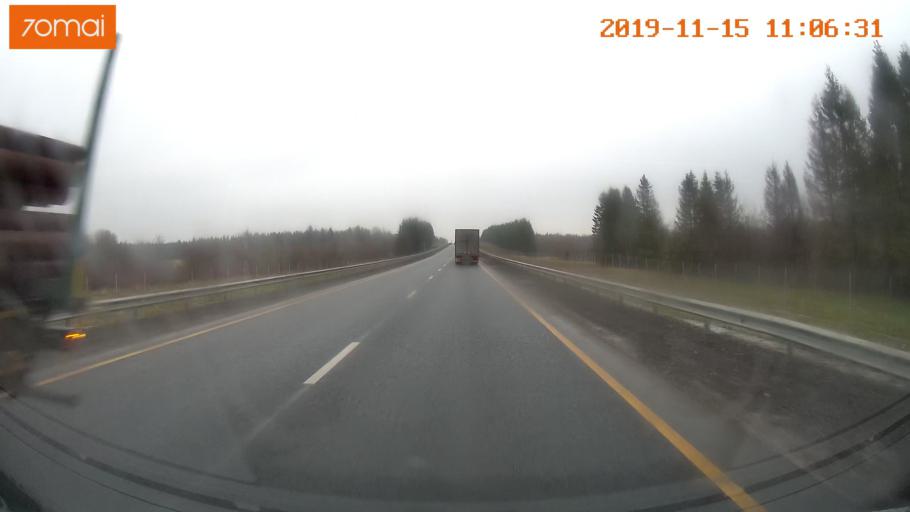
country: RU
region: Vologda
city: Chebsara
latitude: 59.1191
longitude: 39.0296
